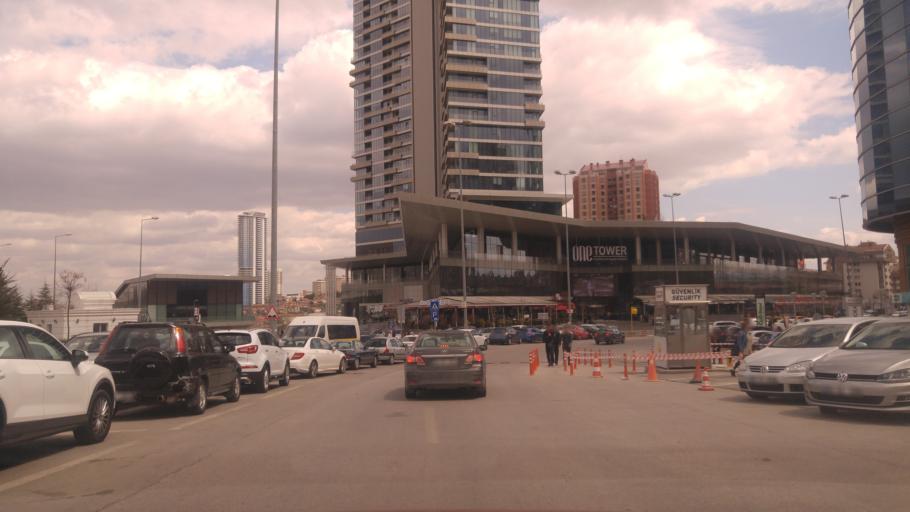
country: TR
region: Ankara
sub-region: Goelbasi
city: Golbasi
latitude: 39.8490
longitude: 32.8335
